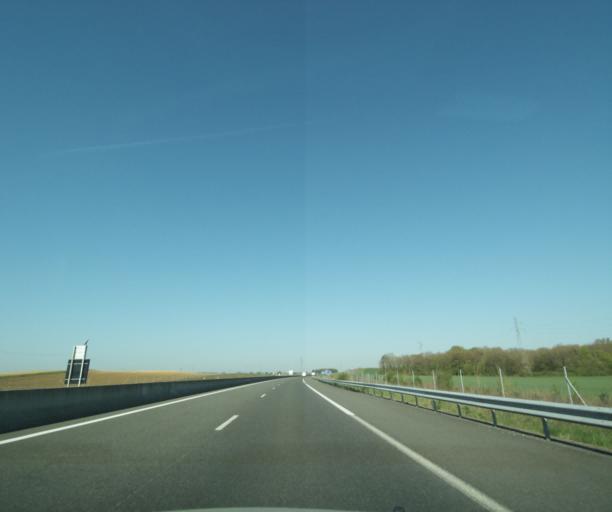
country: FR
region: Centre
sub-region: Departement du Loiret
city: Beaune-la-Rolande
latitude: 48.0832
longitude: 2.4516
